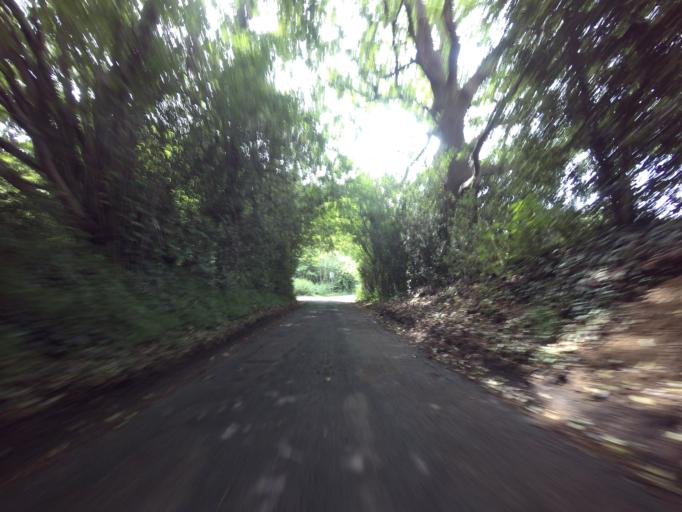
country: GB
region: England
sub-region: Kent
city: Halstead
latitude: 51.3501
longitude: 0.1411
